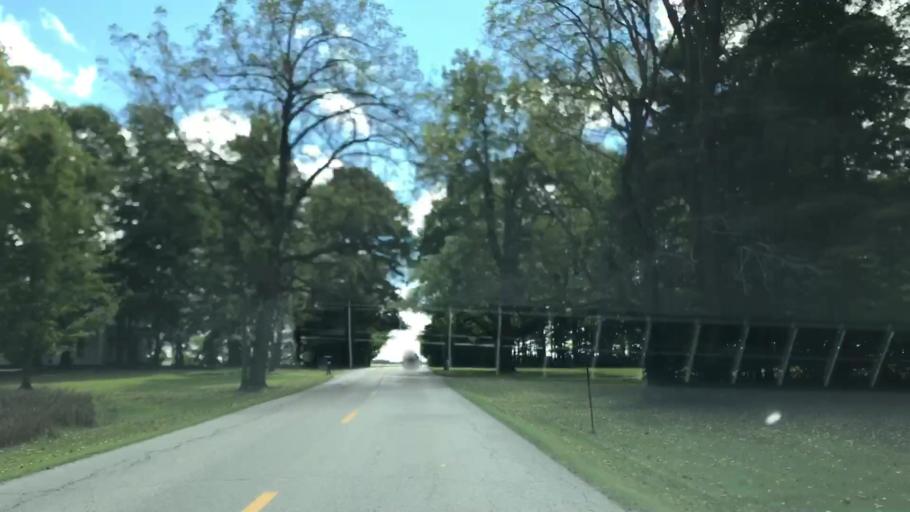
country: US
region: Indiana
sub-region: Howard County
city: Indian Heights
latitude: 40.4240
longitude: -86.0974
